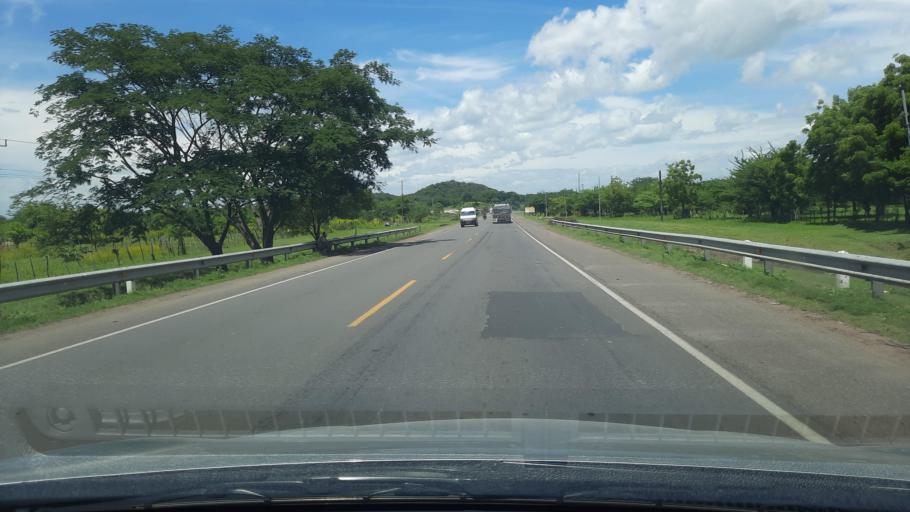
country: NI
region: Chinandega
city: Somotillo
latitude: 13.0553
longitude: -86.9188
